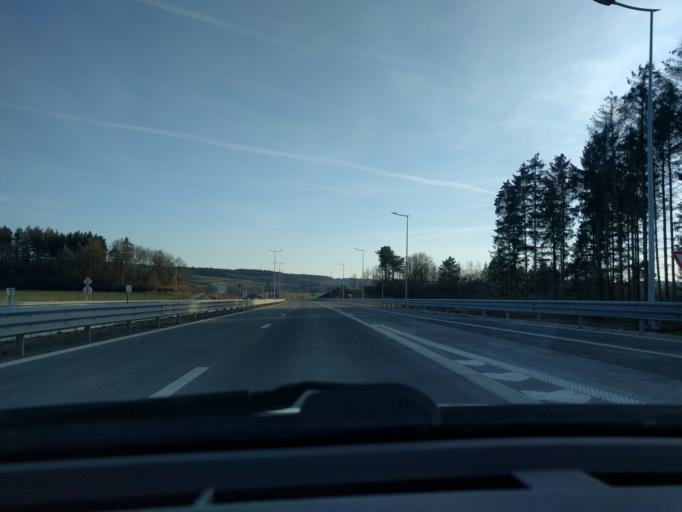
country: BE
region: Wallonia
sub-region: Province de Namur
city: Couvin
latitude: 50.0603
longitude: 4.5055
